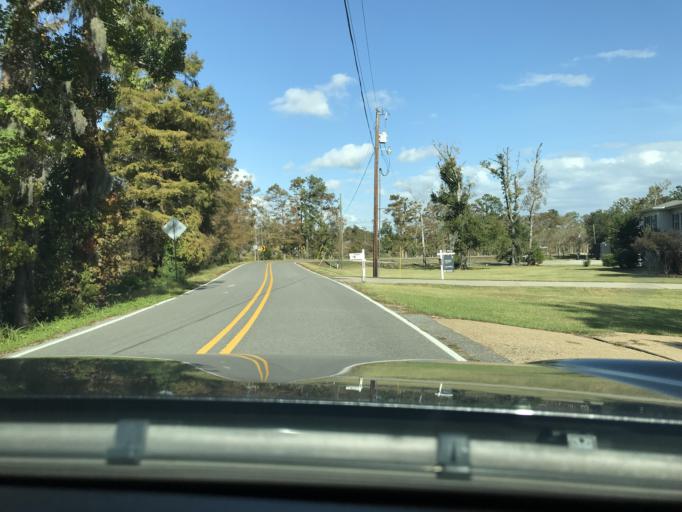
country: US
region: Louisiana
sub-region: Calcasieu Parish
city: Westlake
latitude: 30.3167
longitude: -93.2947
